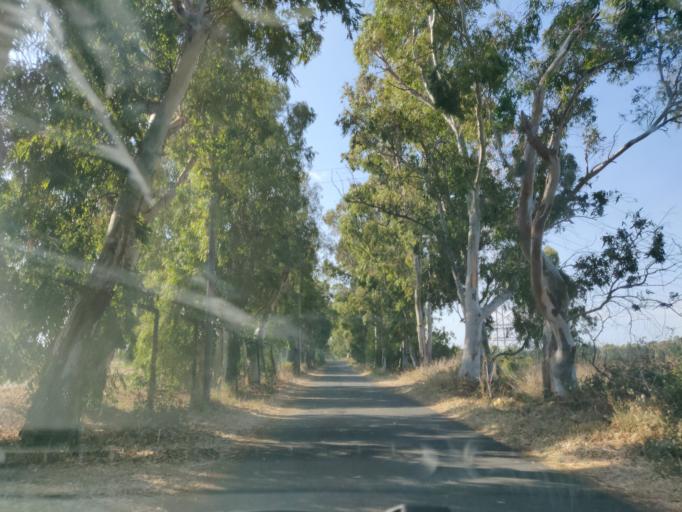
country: IT
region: Latium
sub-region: Citta metropolitana di Roma Capitale
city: Aurelia
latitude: 42.1308
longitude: 11.7663
